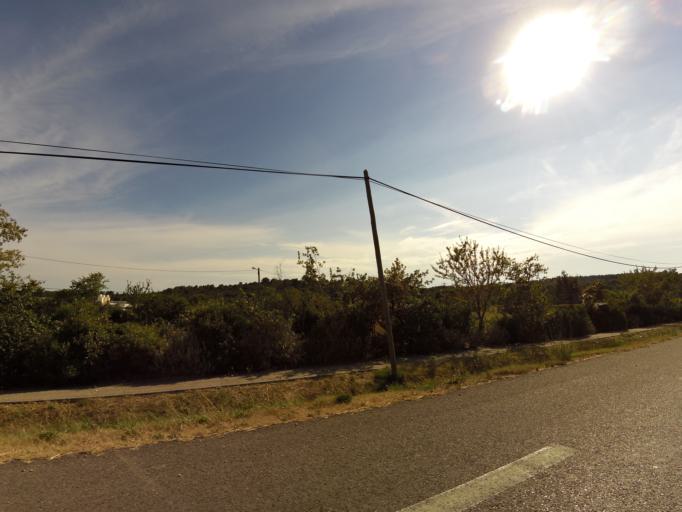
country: FR
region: Languedoc-Roussillon
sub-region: Departement du Gard
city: Milhaud
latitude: 43.8140
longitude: 4.3063
